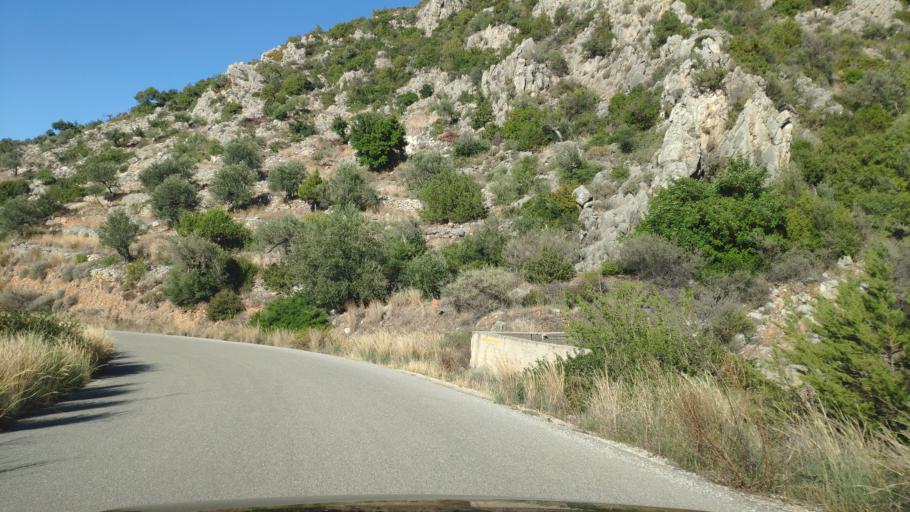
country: GR
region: Attica
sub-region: Nomos Piraios
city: Galatas
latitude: 37.5700
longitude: 23.3617
